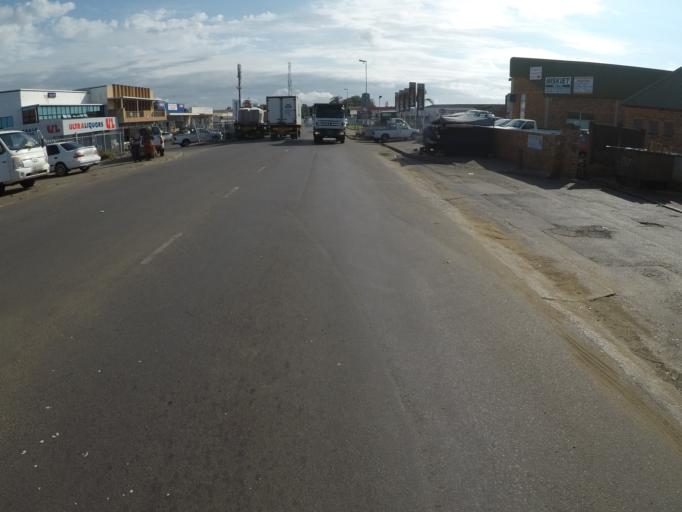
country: ZA
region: KwaZulu-Natal
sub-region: uThungulu District Municipality
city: Empangeni
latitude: -28.7718
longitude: 31.9042
